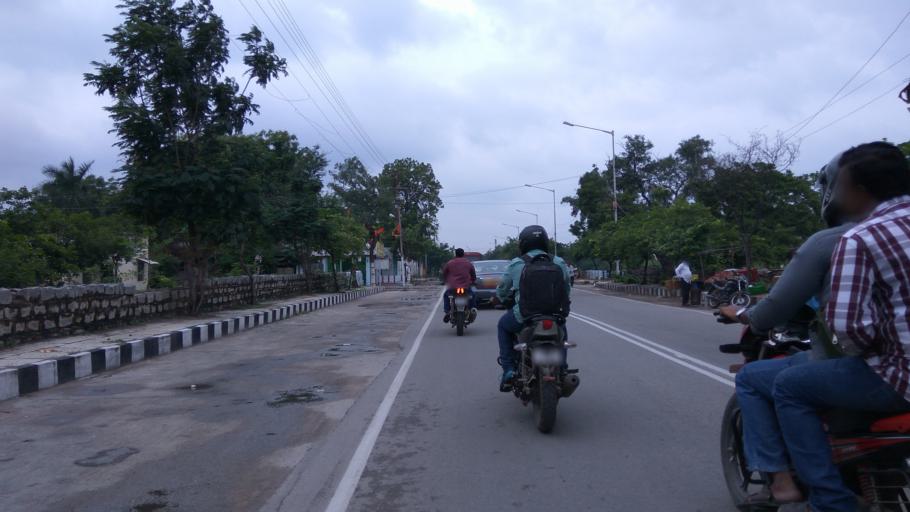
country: IN
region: Telangana
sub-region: Hyderabad
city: Malkajgiri
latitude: 17.4393
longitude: 78.5270
